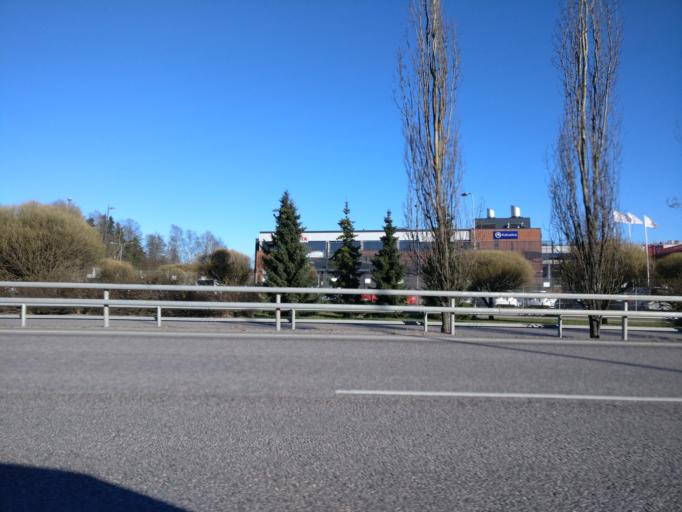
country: FI
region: Uusimaa
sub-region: Helsinki
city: Vantaa
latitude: 60.2117
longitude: 25.0865
